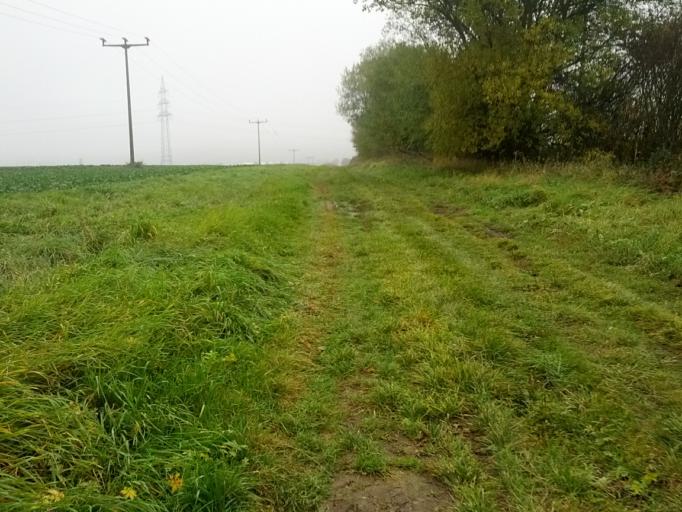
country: DE
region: Thuringia
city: Bischofroda
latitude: 51.0012
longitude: 10.3726
